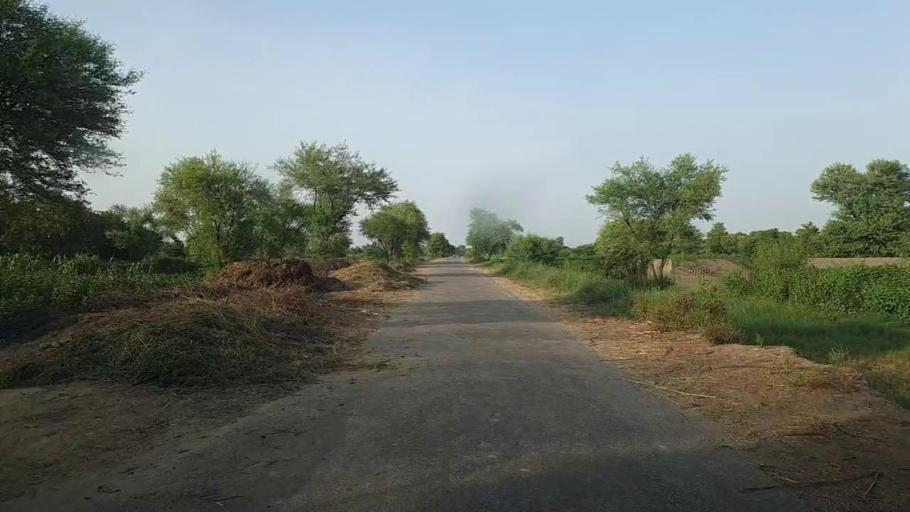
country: PK
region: Sindh
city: Ubauro
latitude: 28.1267
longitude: 69.8304
